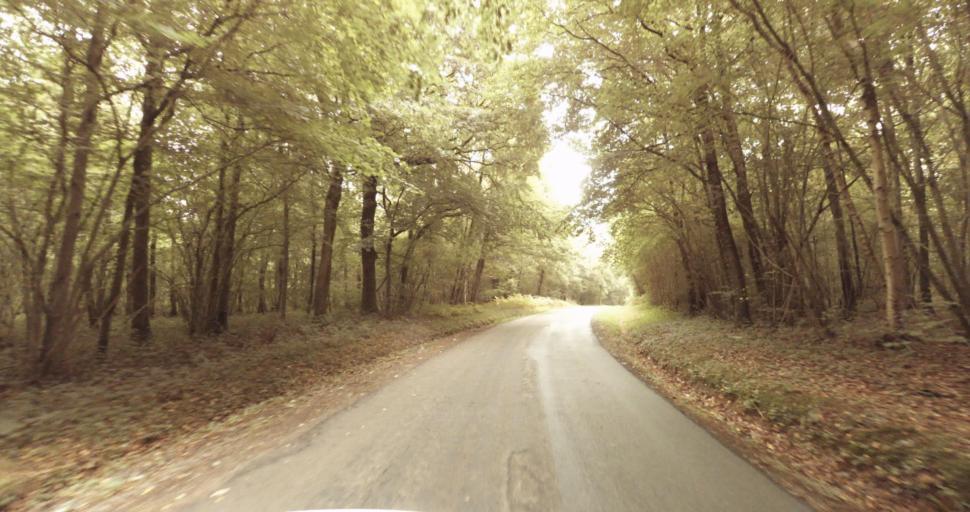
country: FR
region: Lower Normandy
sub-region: Departement de l'Orne
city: Trun
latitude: 48.9033
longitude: 0.1059
